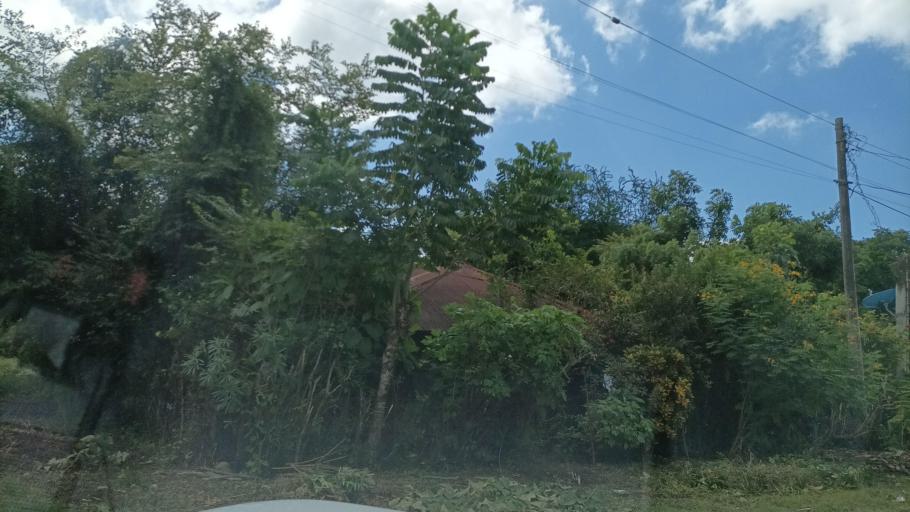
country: MX
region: Veracruz
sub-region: Tantoyuca
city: El Lindero
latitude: 21.1950
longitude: -98.1431
